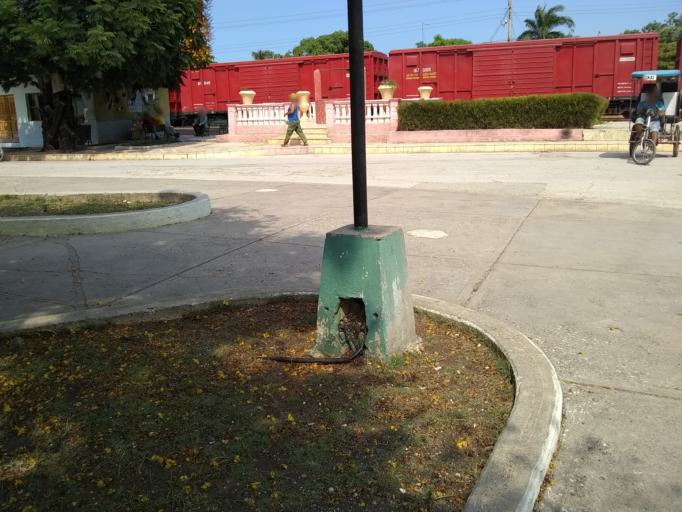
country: CU
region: Holguin
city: Cueto
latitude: 20.6454
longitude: -75.9367
